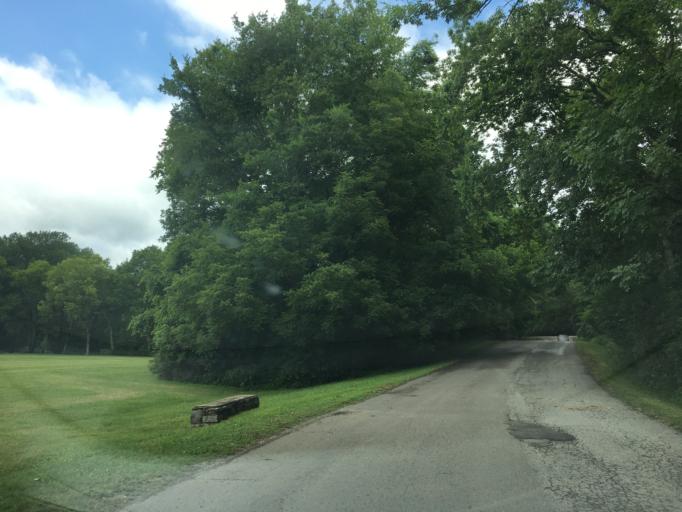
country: US
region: Tennessee
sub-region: Davidson County
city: Forest Hills
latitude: 36.0501
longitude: -86.9071
